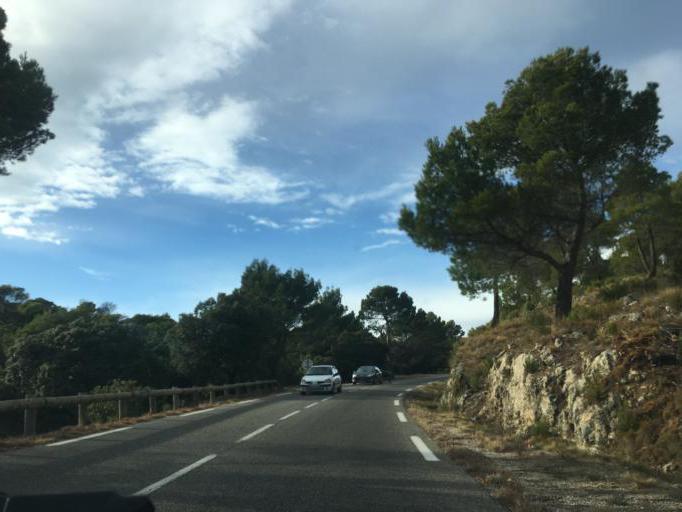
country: FR
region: Provence-Alpes-Cote d'Azur
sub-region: Departement du Var
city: Villecroze
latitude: 43.5860
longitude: 6.2631
